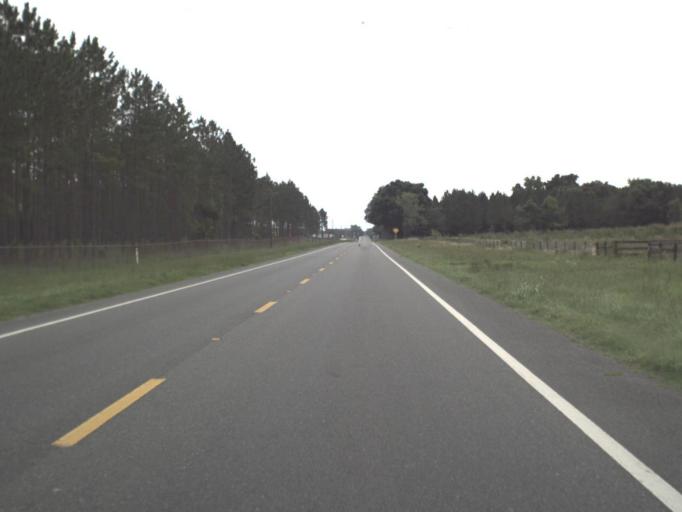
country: US
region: Florida
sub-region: Levy County
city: Williston
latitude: 29.3643
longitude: -82.4558
